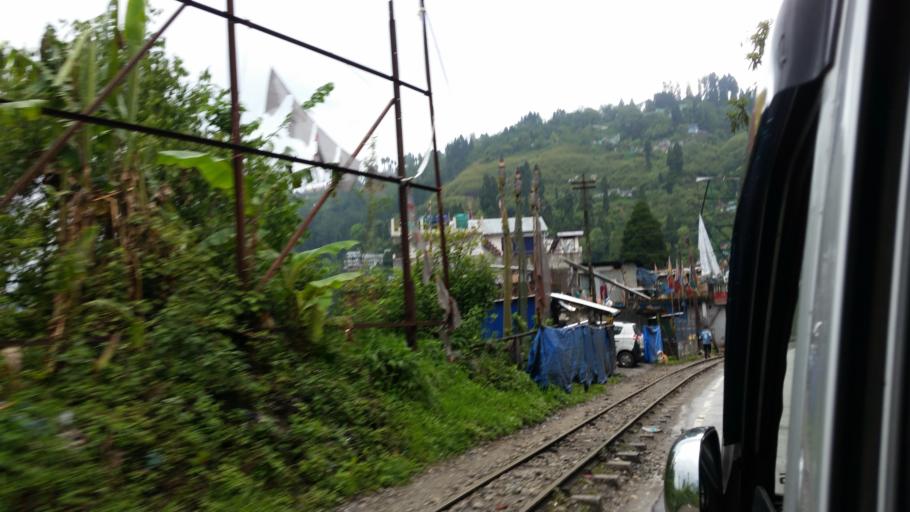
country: IN
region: West Bengal
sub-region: Darjiling
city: Darjiling
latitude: 27.0205
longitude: 88.2507
